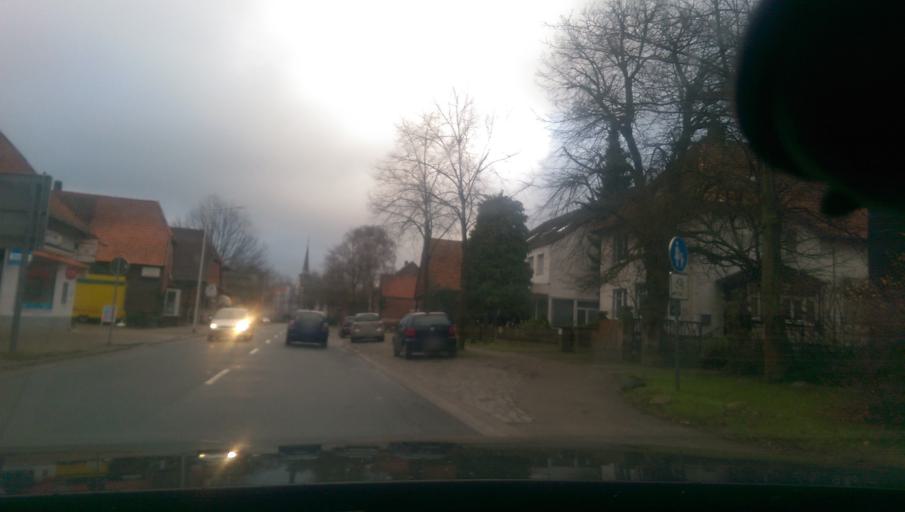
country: DE
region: Lower Saxony
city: Arpke
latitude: 52.3950
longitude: 10.0606
